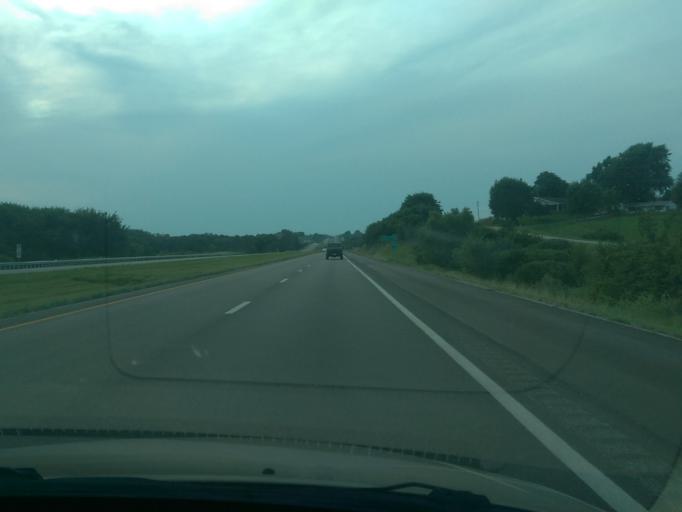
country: US
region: Missouri
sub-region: Andrew County
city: Country Club Village
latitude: 39.8655
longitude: -94.8224
